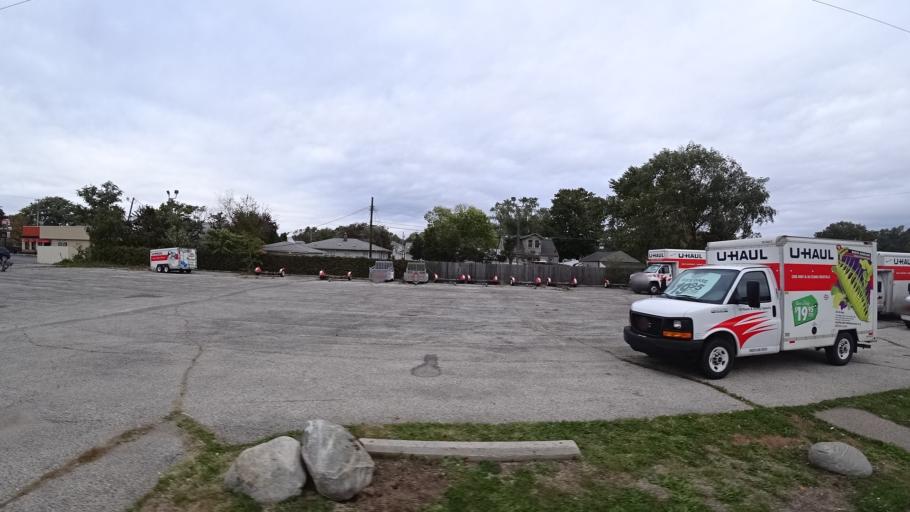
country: US
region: Indiana
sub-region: LaPorte County
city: Michigan City
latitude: 41.7010
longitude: -86.8929
